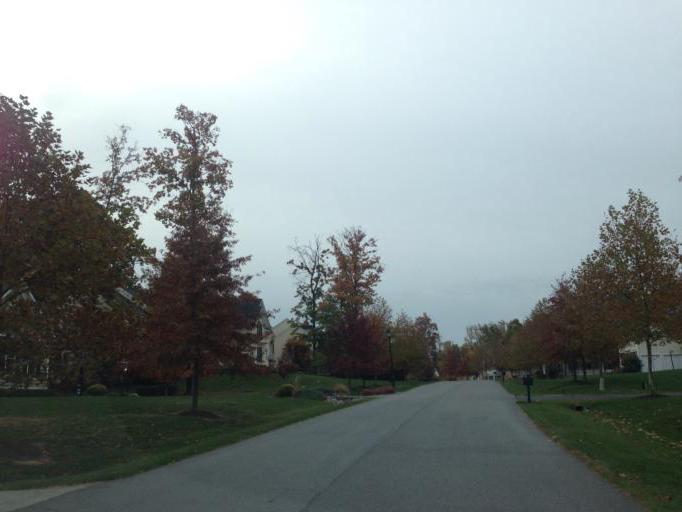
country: US
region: Maryland
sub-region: Howard County
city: Highland
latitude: 39.2556
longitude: -76.9789
